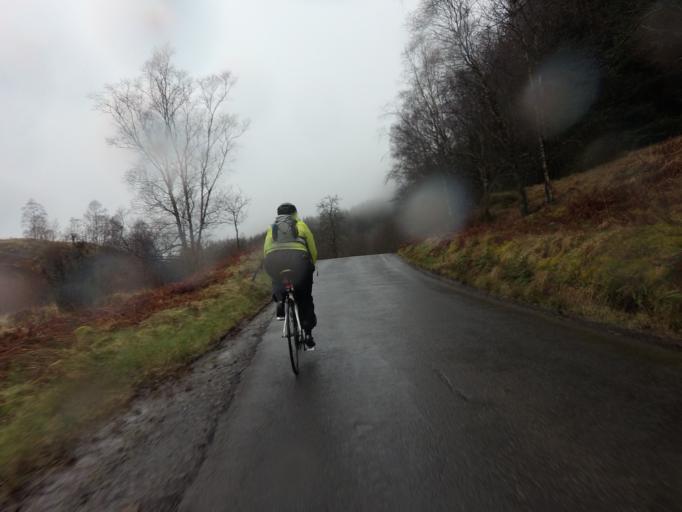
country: GB
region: Scotland
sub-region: West Dunbartonshire
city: Balloch
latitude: 56.2025
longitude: -4.5296
